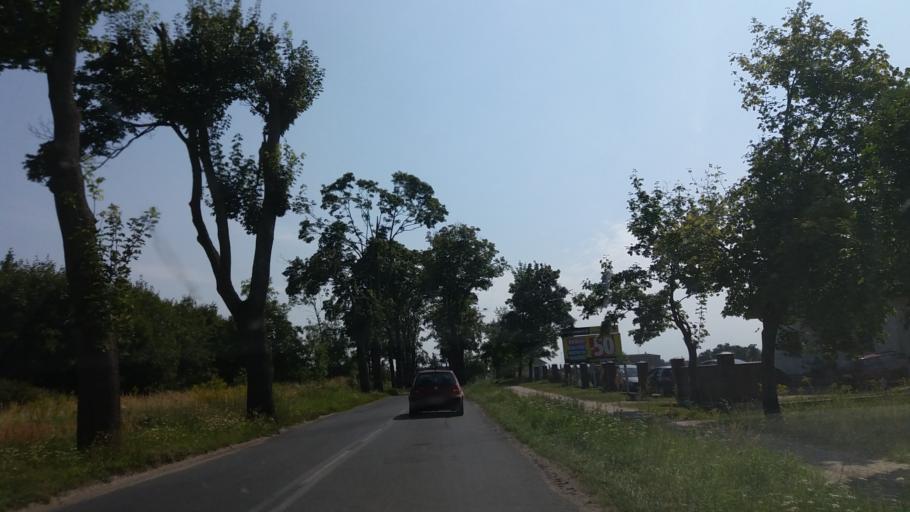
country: PL
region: Lubusz
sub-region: Powiat strzelecko-drezdenecki
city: Strzelce Krajenskie
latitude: 52.8842
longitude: 15.5195
